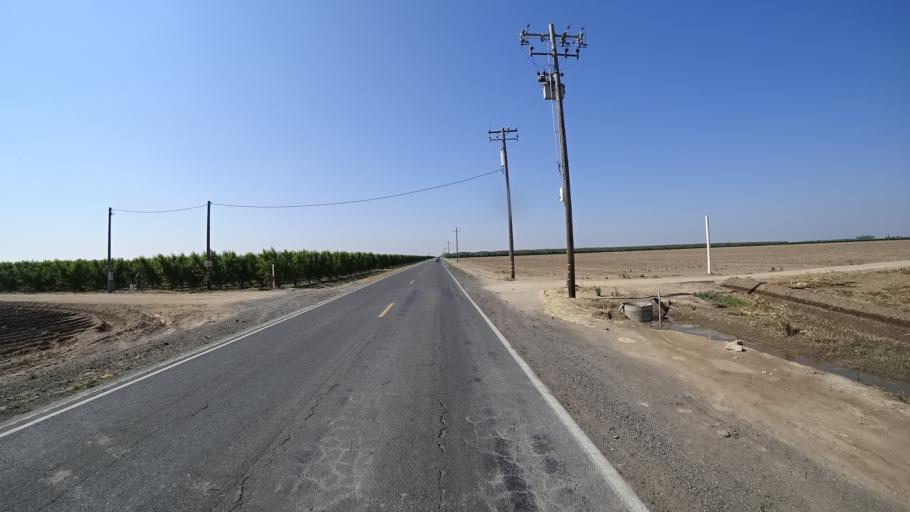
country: US
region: California
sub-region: Kings County
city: Lucerne
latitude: 36.3979
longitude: -119.5650
